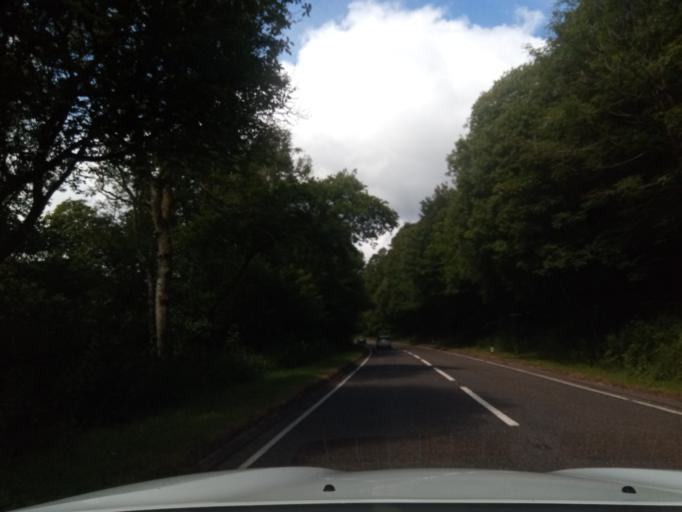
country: GB
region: Scotland
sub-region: Stirling
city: Callander
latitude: 56.2131
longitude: -4.1410
